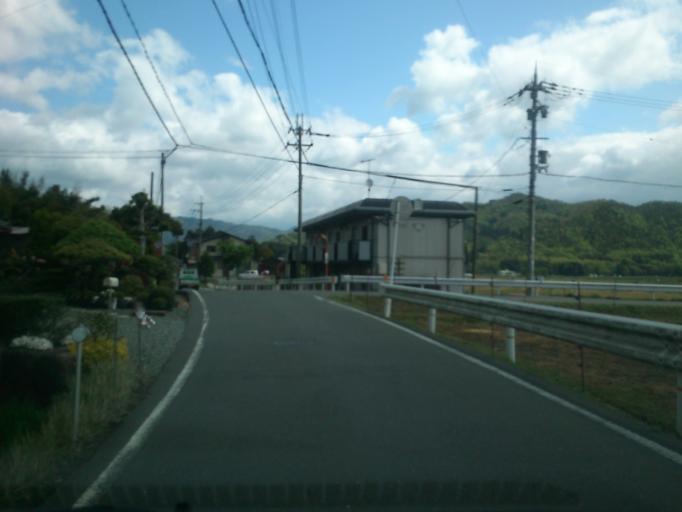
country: JP
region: Kyoto
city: Ayabe
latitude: 35.1838
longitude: 135.4123
